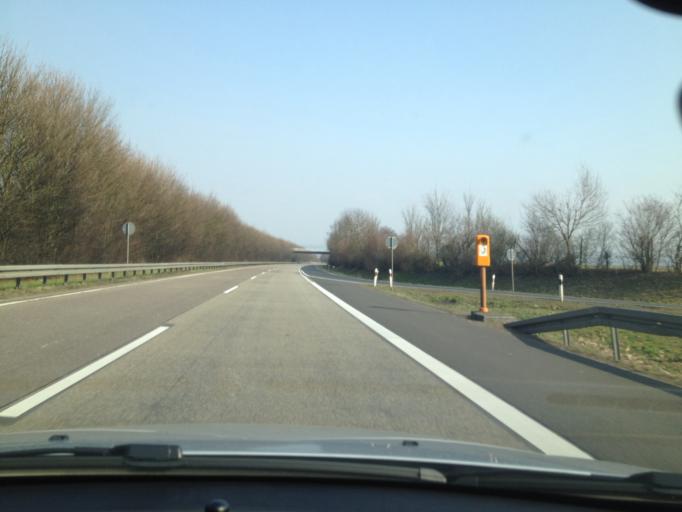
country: DE
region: Hesse
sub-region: Regierungsbezirk Darmstadt
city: Wolfersheim
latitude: 50.4185
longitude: 8.8524
